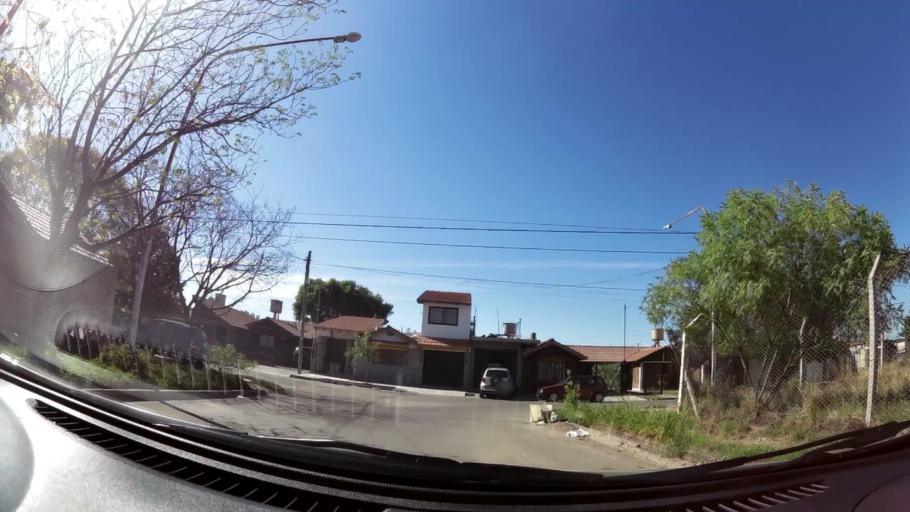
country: AR
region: Mendoza
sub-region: Departamento de Godoy Cruz
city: Godoy Cruz
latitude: -32.9509
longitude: -68.8140
